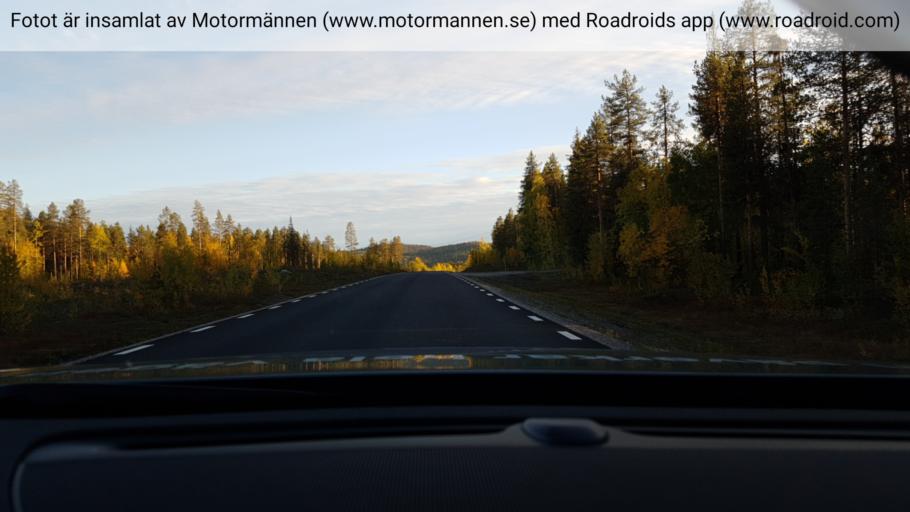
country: SE
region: Norrbotten
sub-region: Jokkmokks Kommun
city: Jokkmokk
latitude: 66.5822
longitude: 19.8033
